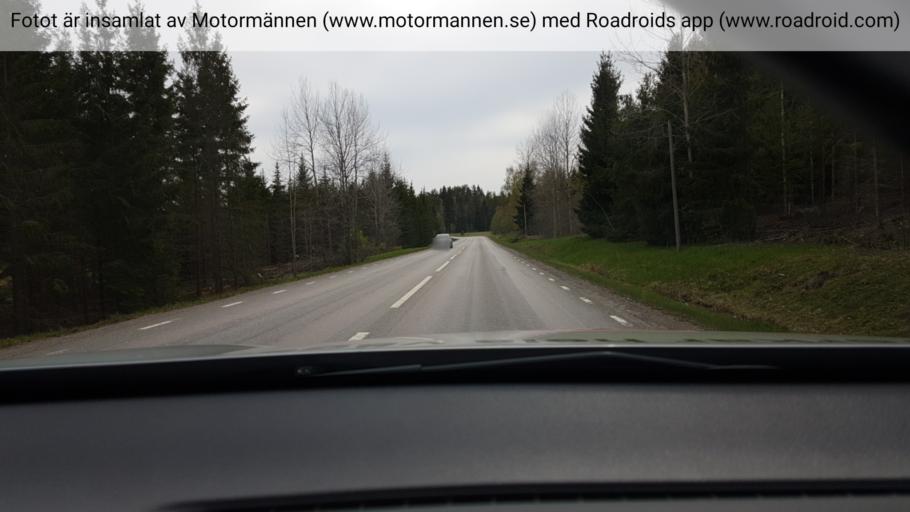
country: SE
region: Stockholm
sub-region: Norrtalje Kommun
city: Nykvarn
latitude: 59.8800
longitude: 18.0781
